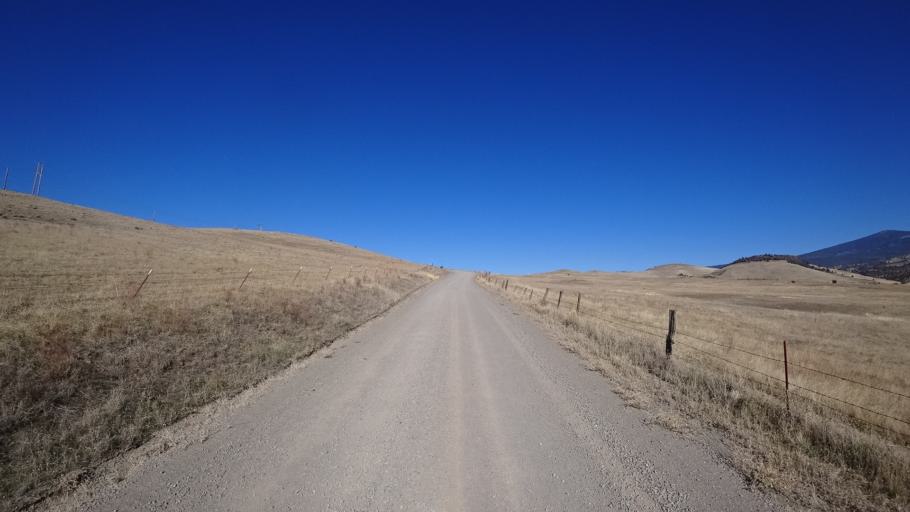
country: US
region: California
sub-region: Siskiyou County
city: Montague
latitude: 41.7644
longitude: -122.3569
